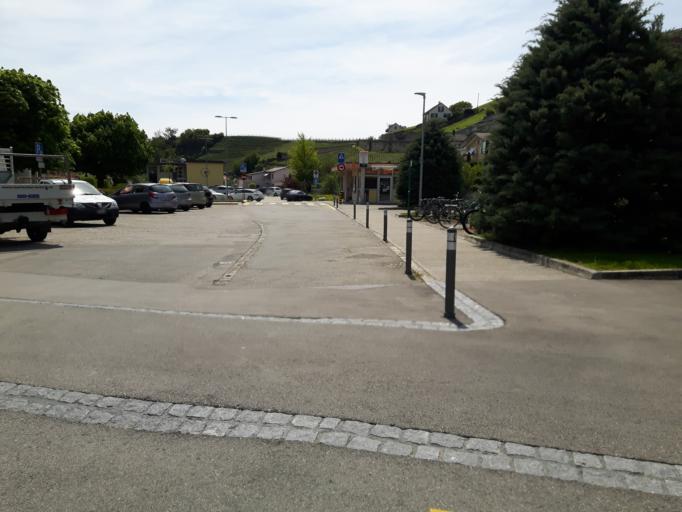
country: CH
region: Neuchatel
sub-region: Boudry District
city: Cortaillod
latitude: 46.9476
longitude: 6.8530
